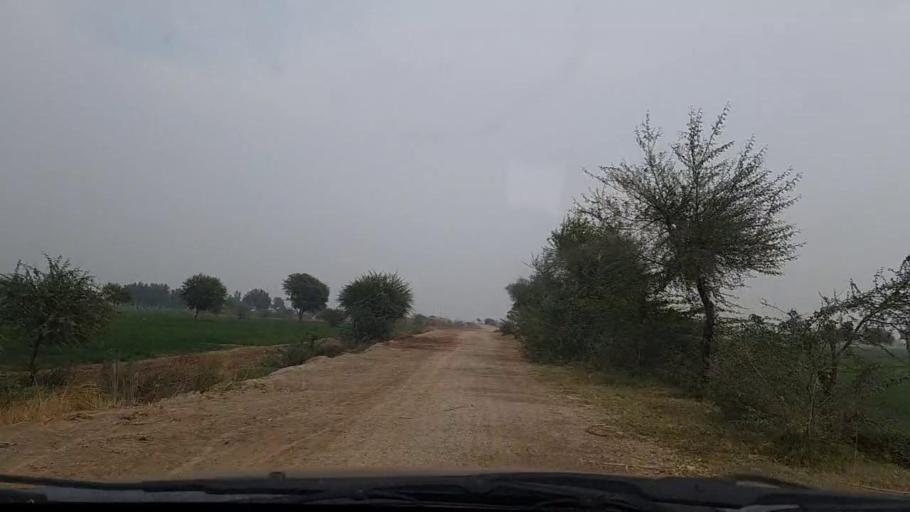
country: PK
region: Sindh
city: Pithoro
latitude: 25.7683
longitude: 69.3874
